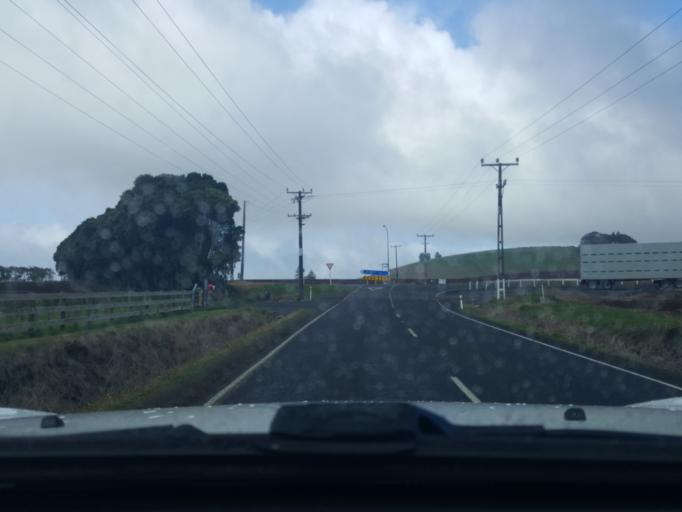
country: NZ
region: Auckland
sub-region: Auckland
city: Pukekohe East
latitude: -37.3257
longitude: 174.9863
